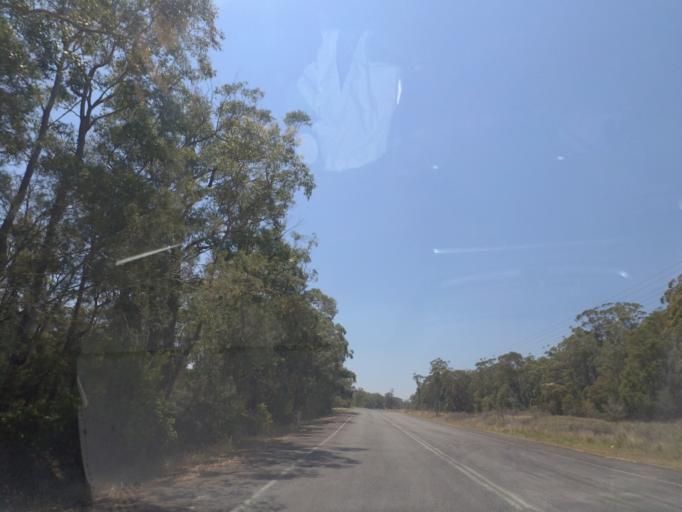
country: AU
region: New South Wales
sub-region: Port Stephens Shire
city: Port Stephens
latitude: -32.6260
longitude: 152.0581
